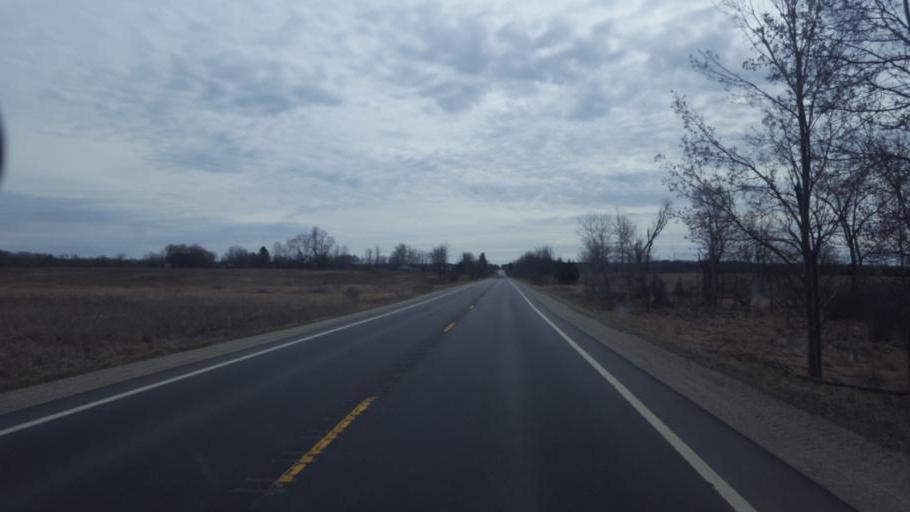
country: US
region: Michigan
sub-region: Isabella County
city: Lake Isabella
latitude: 43.7164
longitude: -85.1467
